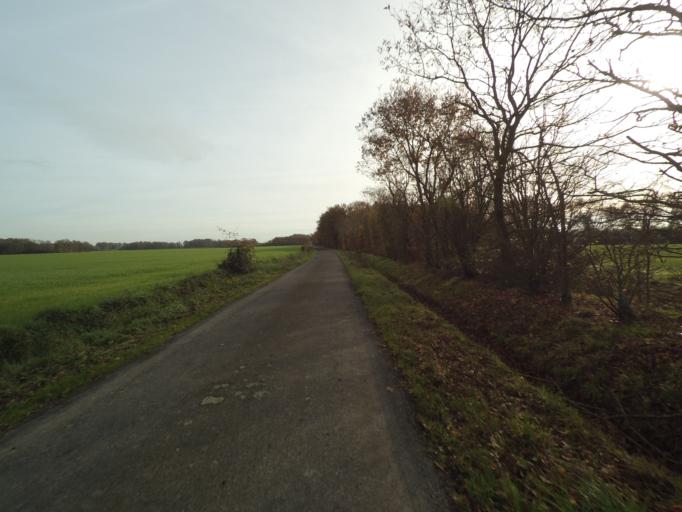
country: FR
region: Pays de la Loire
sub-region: Departement de la Loire-Atlantique
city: La Planche
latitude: 47.0106
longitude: -1.4082
